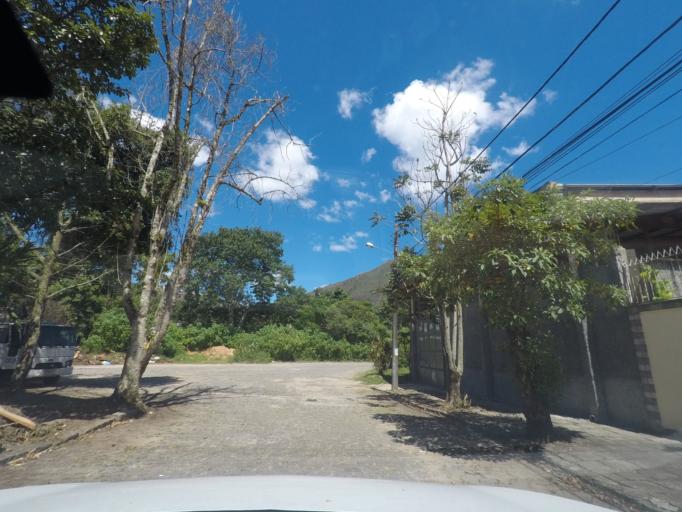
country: BR
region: Rio de Janeiro
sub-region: Teresopolis
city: Teresopolis
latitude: -22.4333
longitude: -42.9753
